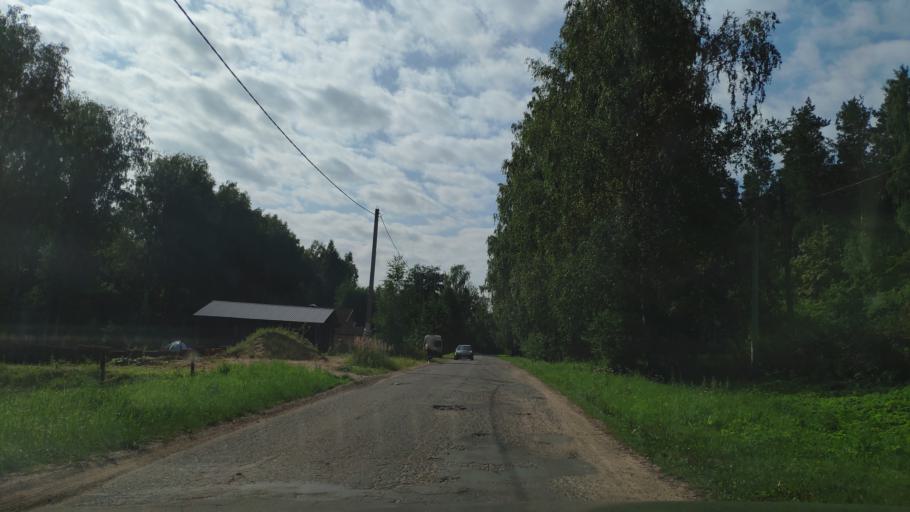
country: BY
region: Minsk
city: Zaslawye
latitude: 53.9875
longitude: 27.2881
